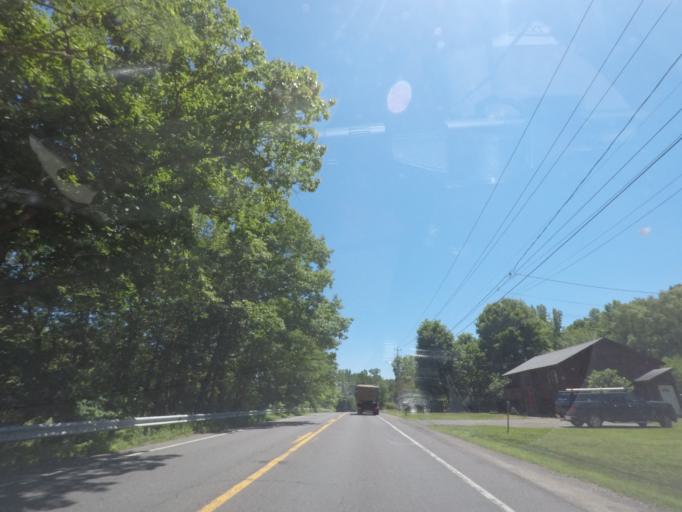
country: US
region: Massachusetts
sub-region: Hampden County
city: Westfield
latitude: 42.1434
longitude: -72.8093
